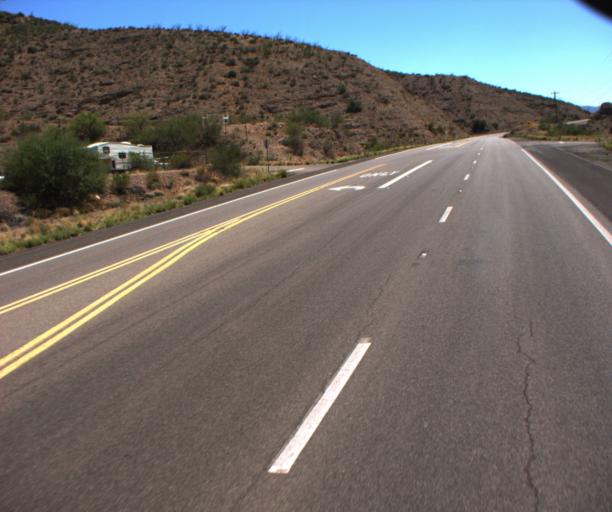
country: US
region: Arizona
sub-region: Greenlee County
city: Clifton
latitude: 33.0371
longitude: -109.2968
